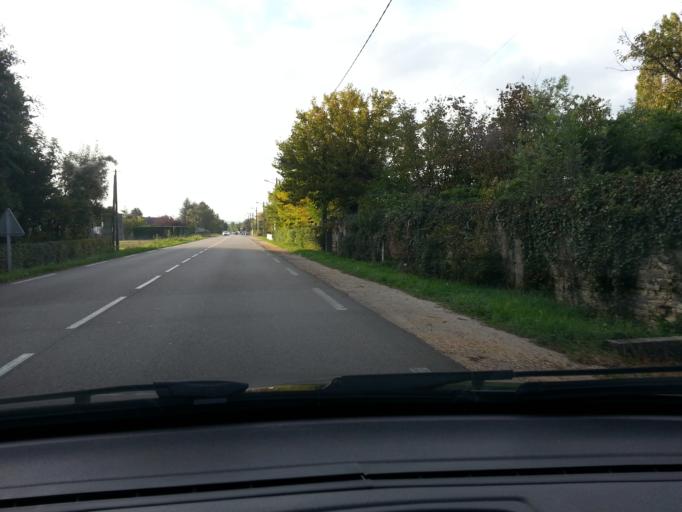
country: FR
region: Bourgogne
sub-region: Departement de Saone-et-Loire
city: Chatenoy-le-Royal
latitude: 46.7750
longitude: 4.8130
